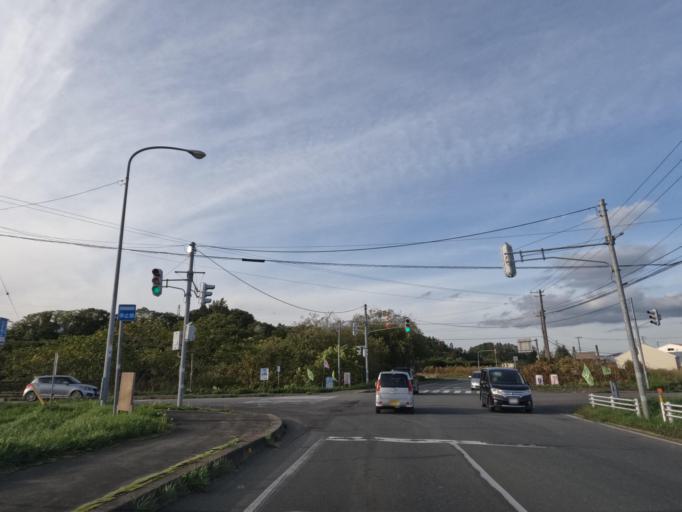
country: JP
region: Hokkaido
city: Date
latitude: 42.5047
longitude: 140.8742
